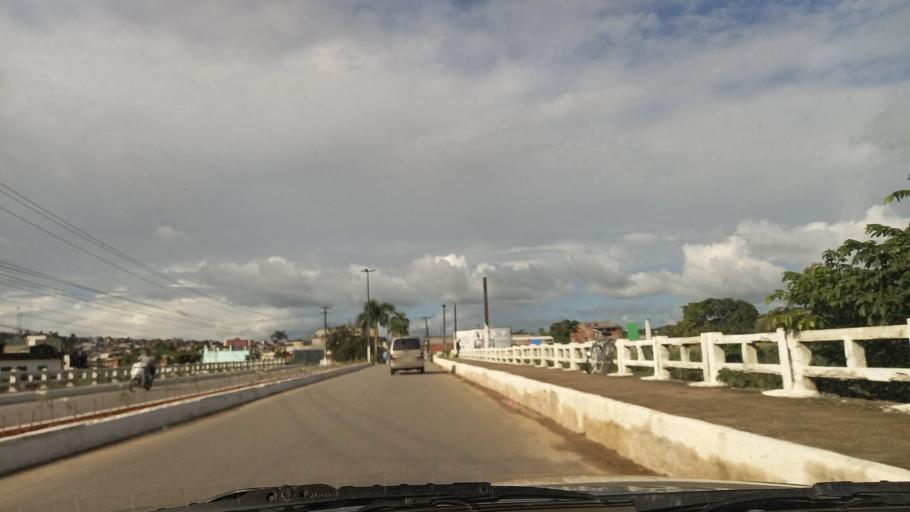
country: BR
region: Pernambuco
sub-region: Palmares
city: Palmares
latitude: -8.6887
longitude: -35.6001
